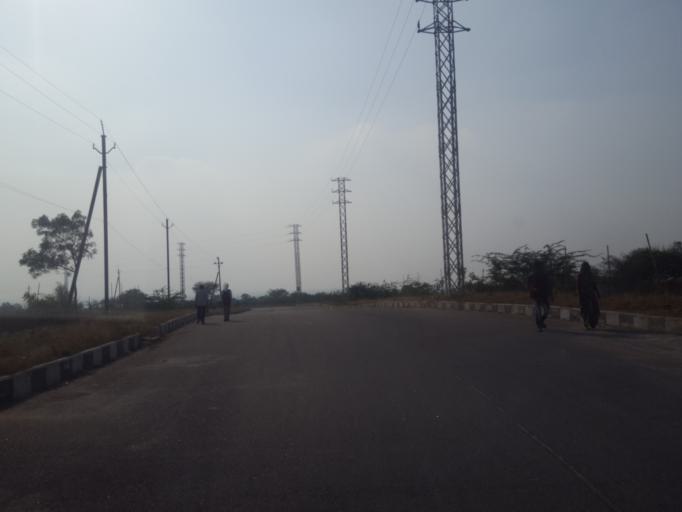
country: IN
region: Telangana
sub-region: Medak
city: Serilingampalle
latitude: 17.4035
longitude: 78.3127
